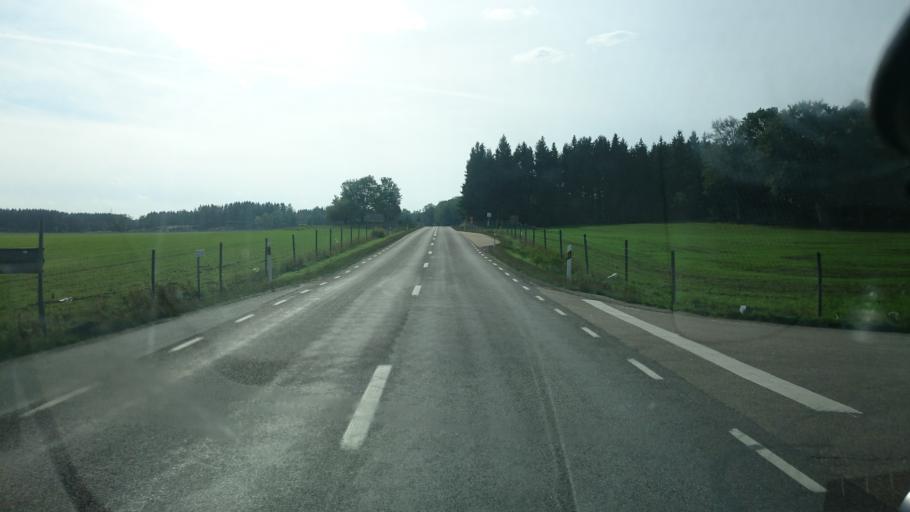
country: SE
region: Vaestra Goetaland
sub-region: Alingsas Kommun
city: Sollebrunn
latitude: 58.1715
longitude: 12.4167
